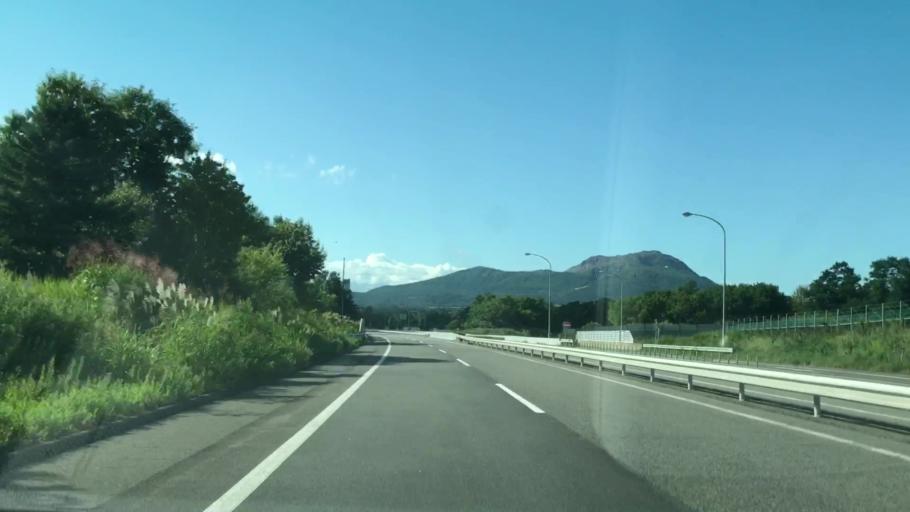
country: JP
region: Hokkaido
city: Date
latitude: 42.4835
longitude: 140.8948
